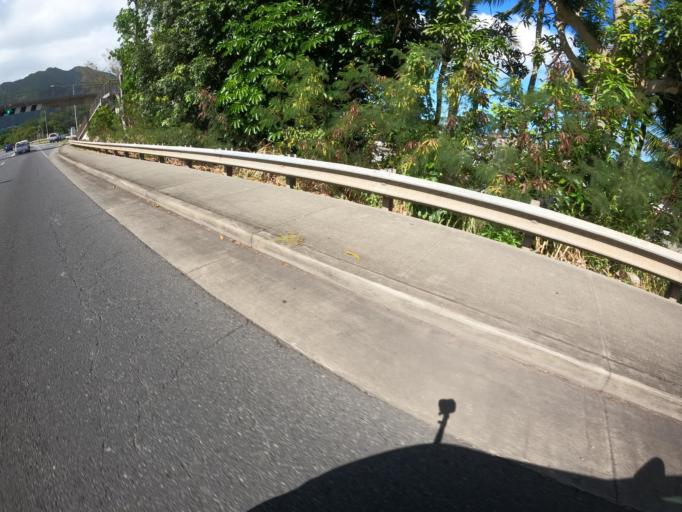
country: US
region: Hawaii
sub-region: Honolulu County
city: Kane'ohe
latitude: 21.4037
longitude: -157.8026
